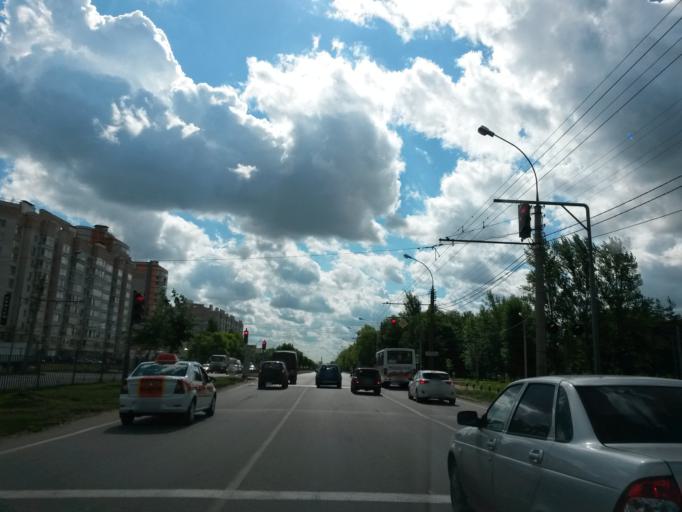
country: RU
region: Jaroslavl
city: Yaroslavl
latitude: 57.6897
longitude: 39.7778
